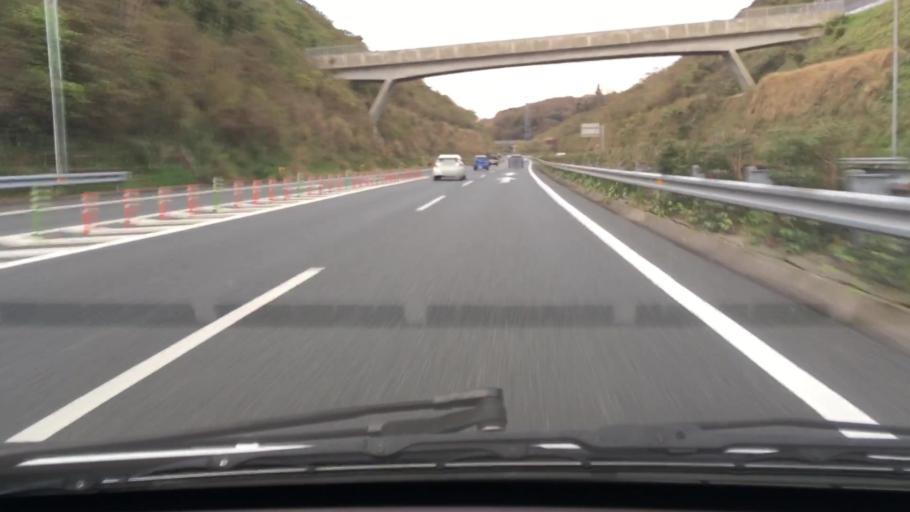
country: JP
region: Chiba
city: Kimitsu
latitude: 35.3215
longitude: 139.9446
